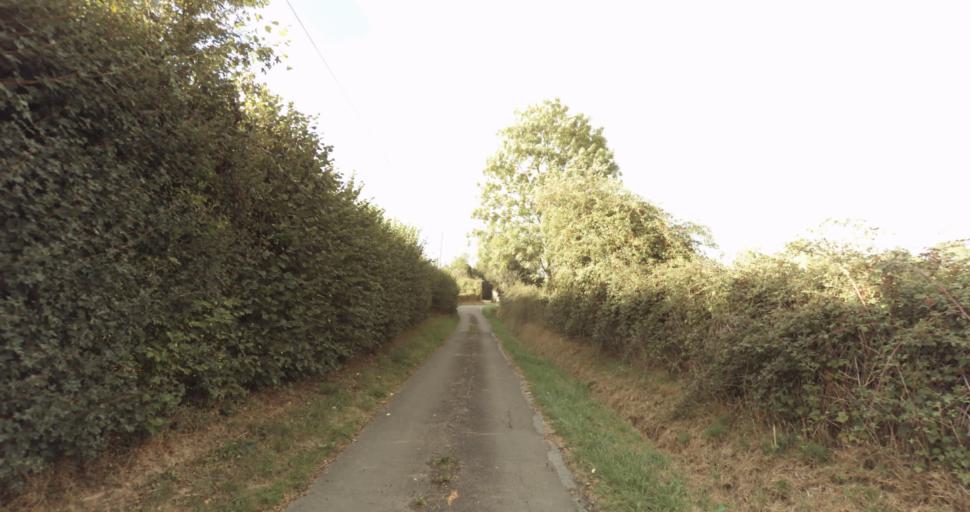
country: FR
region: Lower Normandy
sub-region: Departement de l'Orne
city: Sainte-Gauburge-Sainte-Colombe
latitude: 48.7177
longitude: 0.4140
